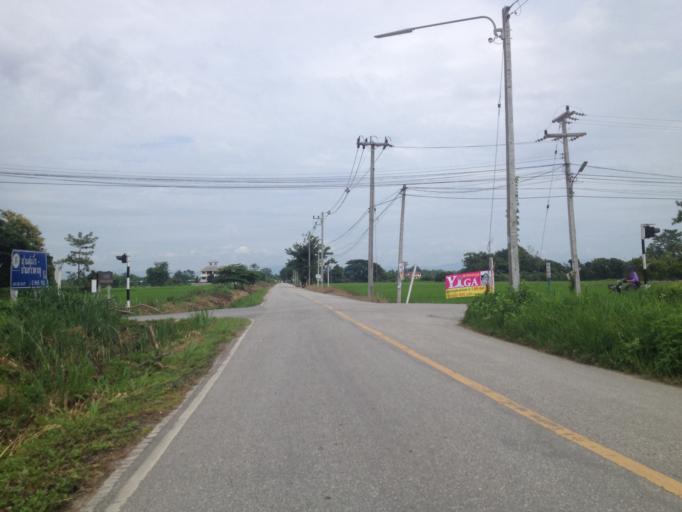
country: TH
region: Chiang Mai
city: Hang Dong
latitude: 18.7026
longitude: 98.9652
